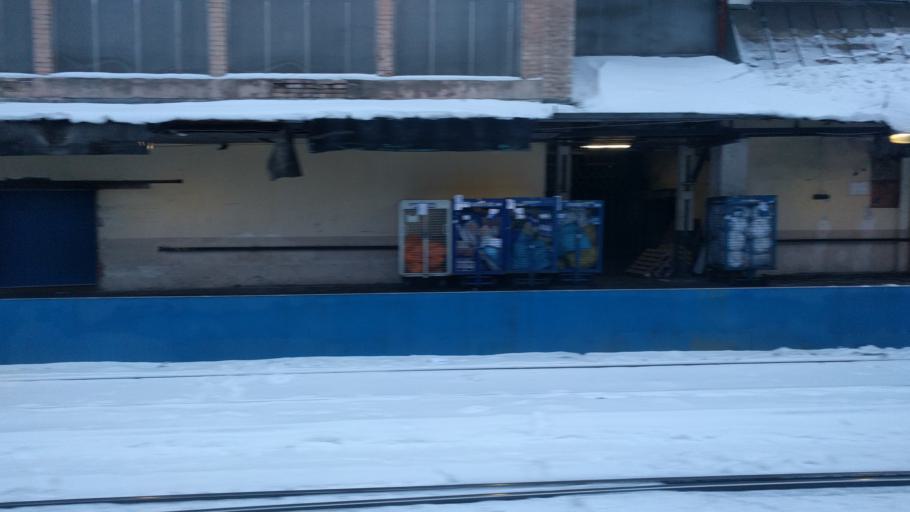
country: RU
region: Moscow
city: Sokol'niki
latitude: 55.7859
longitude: 37.6482
